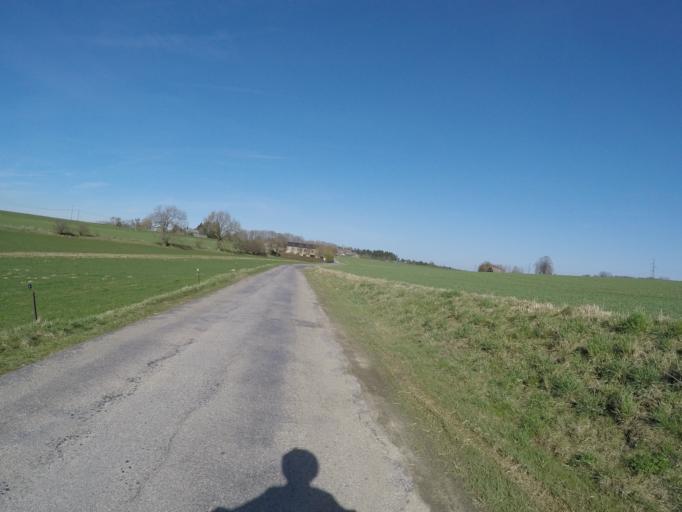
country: BE
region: Wallonia
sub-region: Province de Namur
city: Hamois
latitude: 50.3915
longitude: 5.1582
